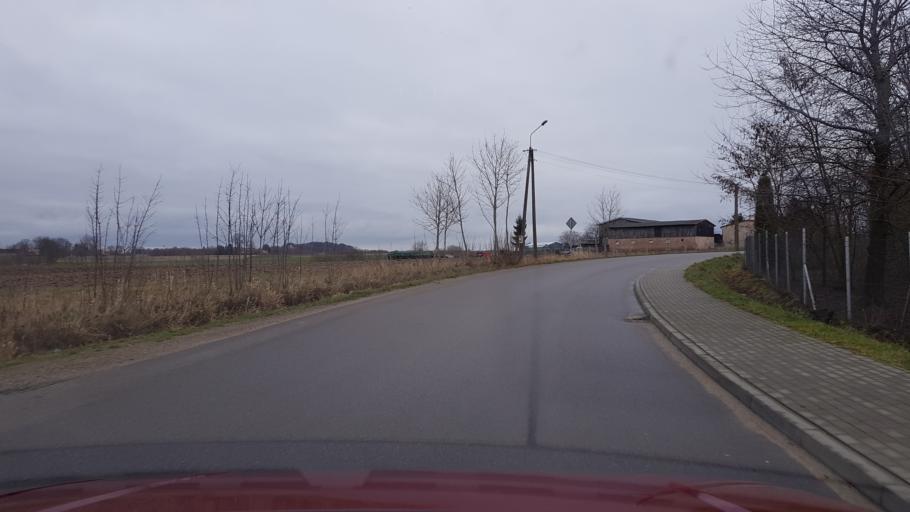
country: PL
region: West Pomeranian Voivodeship
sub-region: Powiat koszalinski
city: Mielno
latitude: 54.1698
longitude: 16.0248
